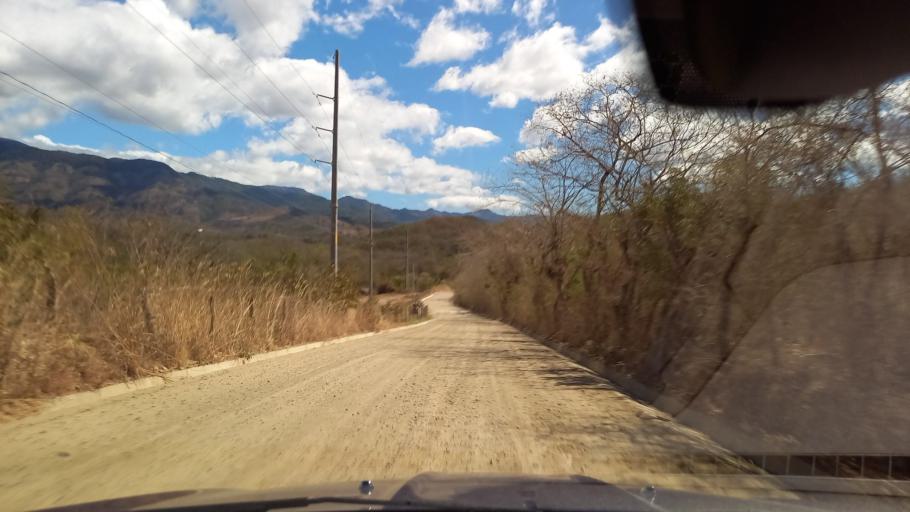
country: SV
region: Santa Ana
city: Metapan
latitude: 14.3602
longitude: -89.4702
